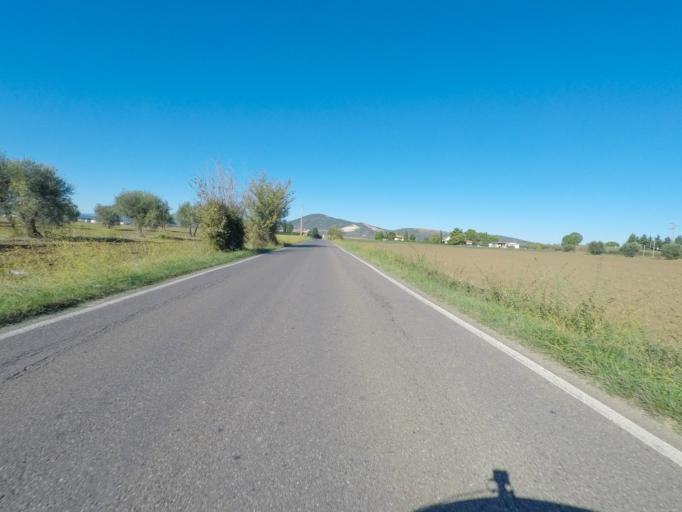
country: IT
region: Tuscany
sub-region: Provincia di Grosseto
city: Grosseto
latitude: 42.7721
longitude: 11.1395
